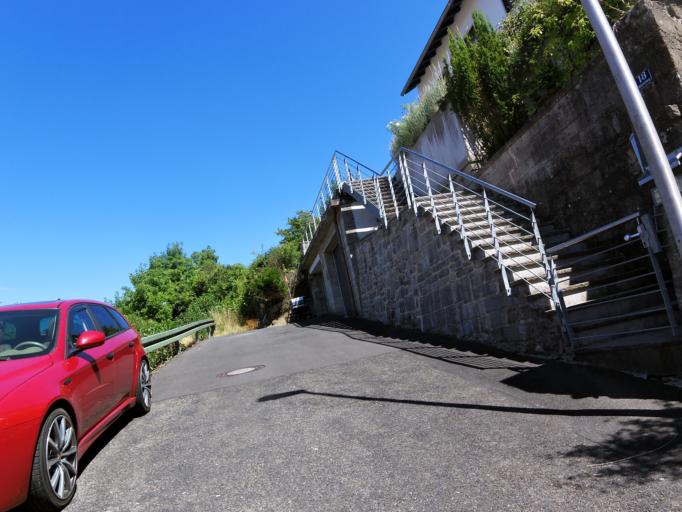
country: DE
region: Bavaria
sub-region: Regierungsbezirk Unterfranken
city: Randersacker
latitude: 49.7604
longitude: 9.9875
